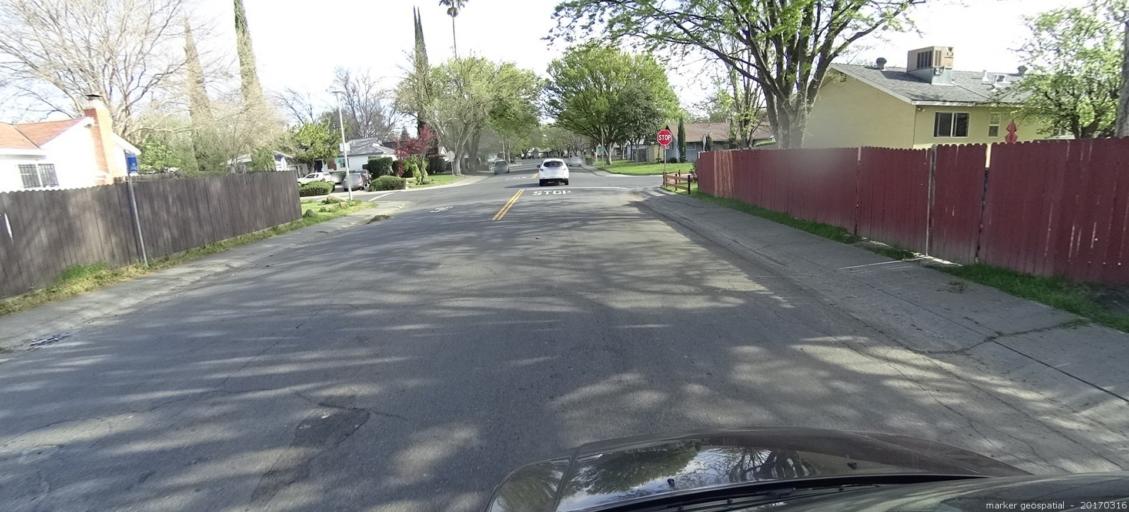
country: US
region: California
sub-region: Sacramento County
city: Parkway
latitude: 38.5064
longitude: -121.4894
